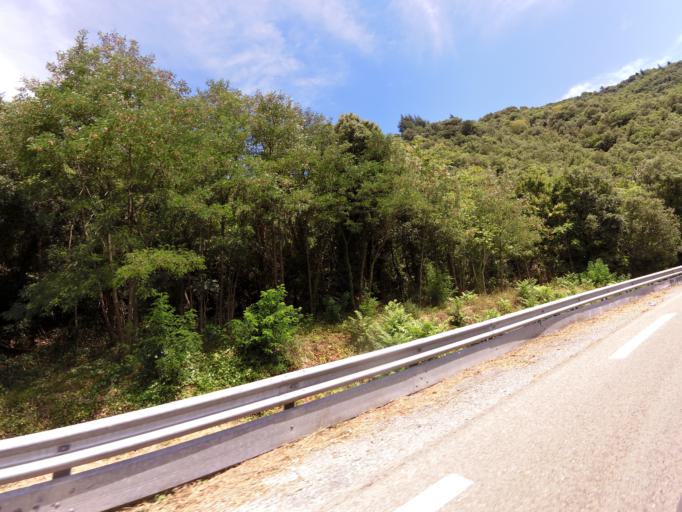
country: FR
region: Languedoc-Roussillon
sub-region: Departement du Gard
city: Sumene
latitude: 43.9822
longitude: 3.6920
